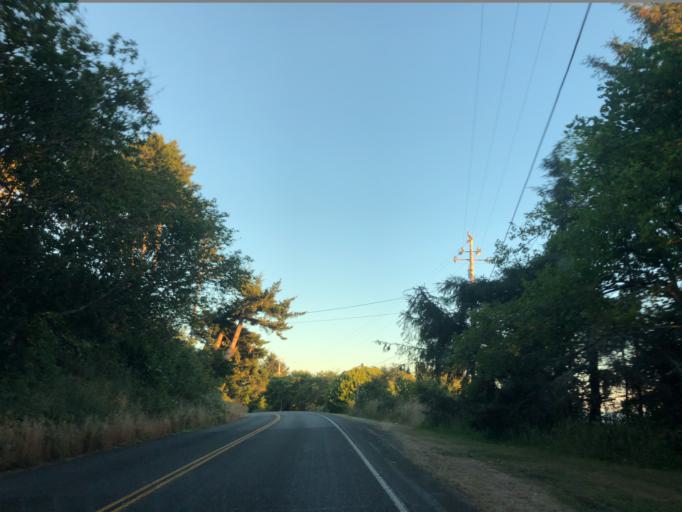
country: US
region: California
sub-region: Humboldt County
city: Westhaven-Moonstone
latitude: 41.0967
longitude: -124.1572
